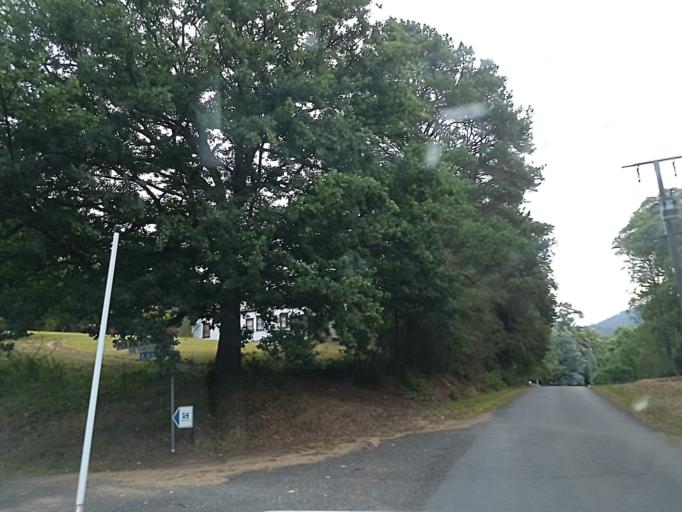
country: AU
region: Victoria
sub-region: Alpine
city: Mount Beauty
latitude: -36.8991
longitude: 147.0585
